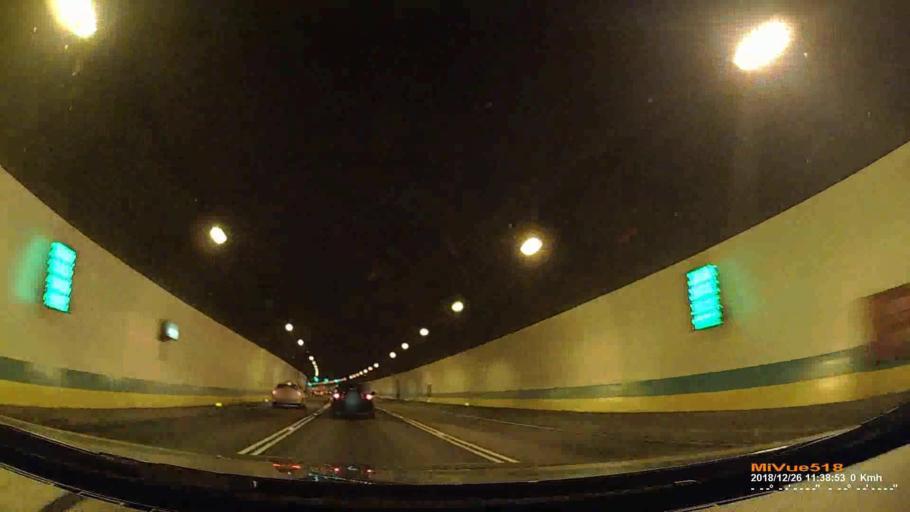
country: TW
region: Taipei
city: Taipei
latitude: 24.9850
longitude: 121.5879
